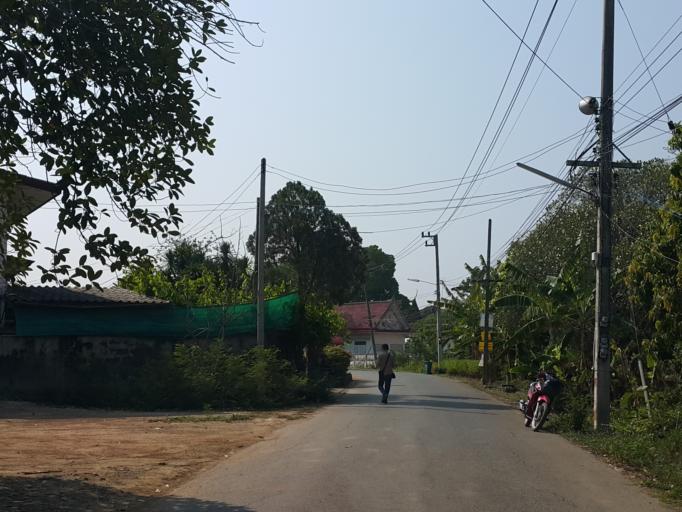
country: TH
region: Kanchanaburi
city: Sai Yok
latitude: 14.1215
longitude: 99.1360
